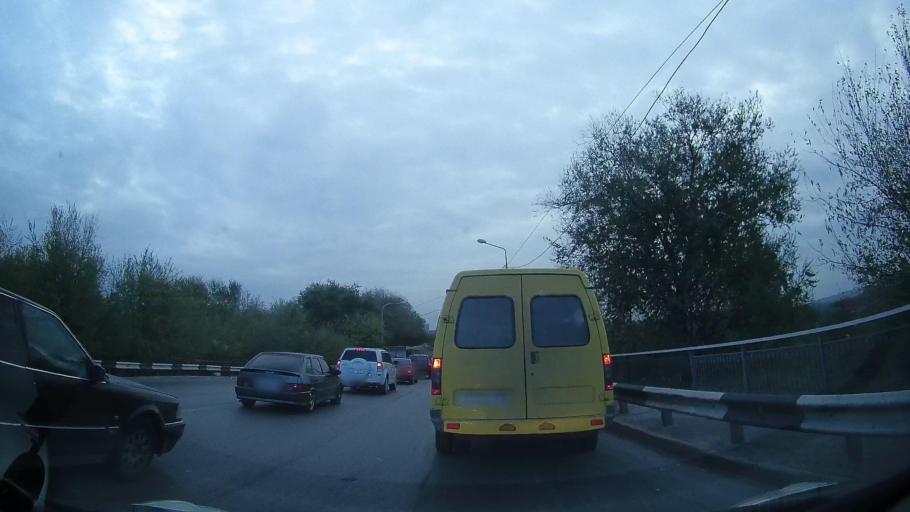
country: RU
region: Rostov
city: Rostov-na-Donu
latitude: 47.2465
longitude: 39.6545
